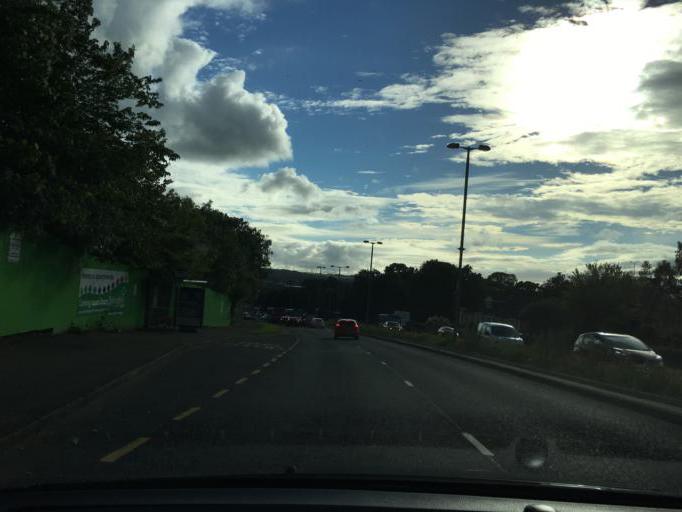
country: GB
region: Scotland
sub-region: North Lanarkshire
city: Motherwell
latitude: 55.7857
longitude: -4.0094
